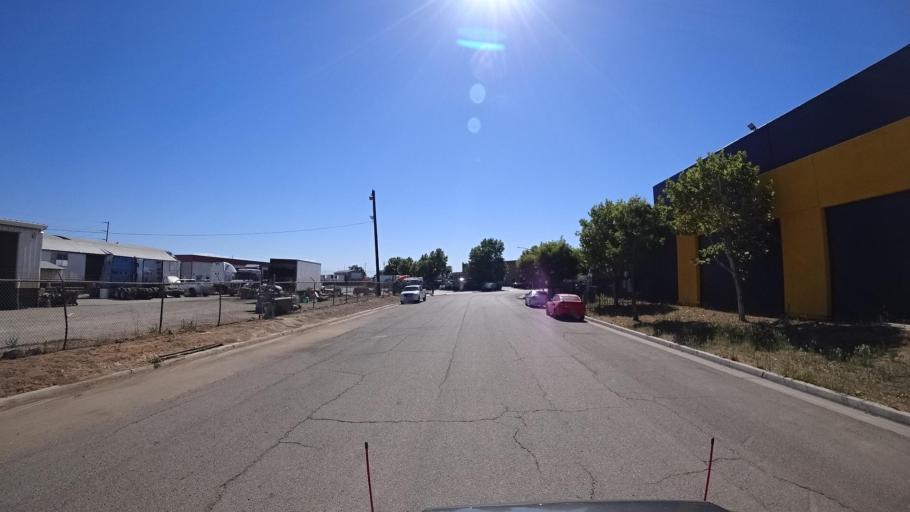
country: US
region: California
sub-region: Fresno County
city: Fresno
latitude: 36.7129
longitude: -119.7777
